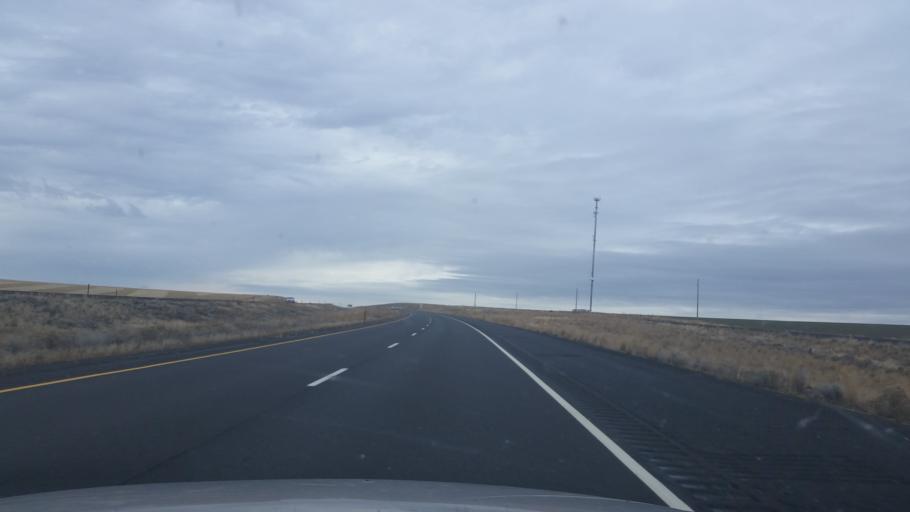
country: US
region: Washington
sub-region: Adams County
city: Ritzville
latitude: 47.0974
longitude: -118.6787
